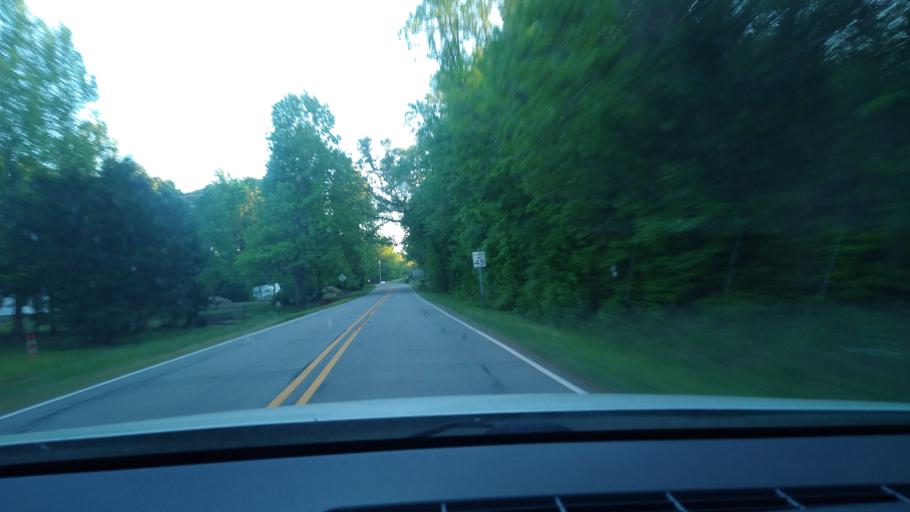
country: US
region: North Carolina
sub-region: Rockingham County
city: Reidsville
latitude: 36.3688
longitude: -79.5515
